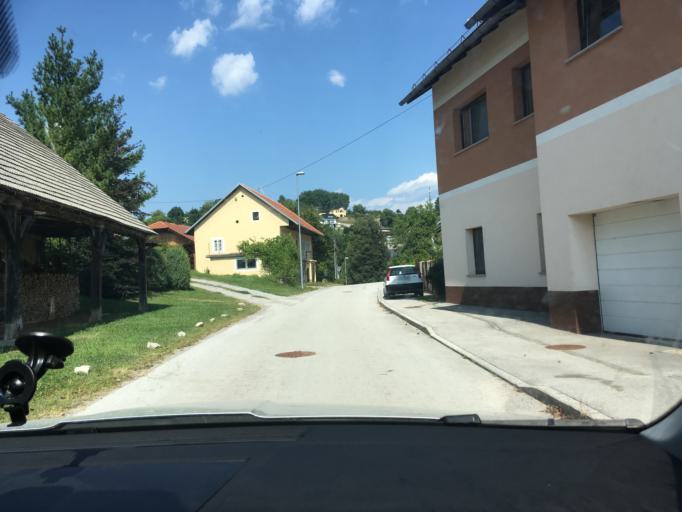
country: SI
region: Metlika
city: Metlika
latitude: 45.6529
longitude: 15.3114
